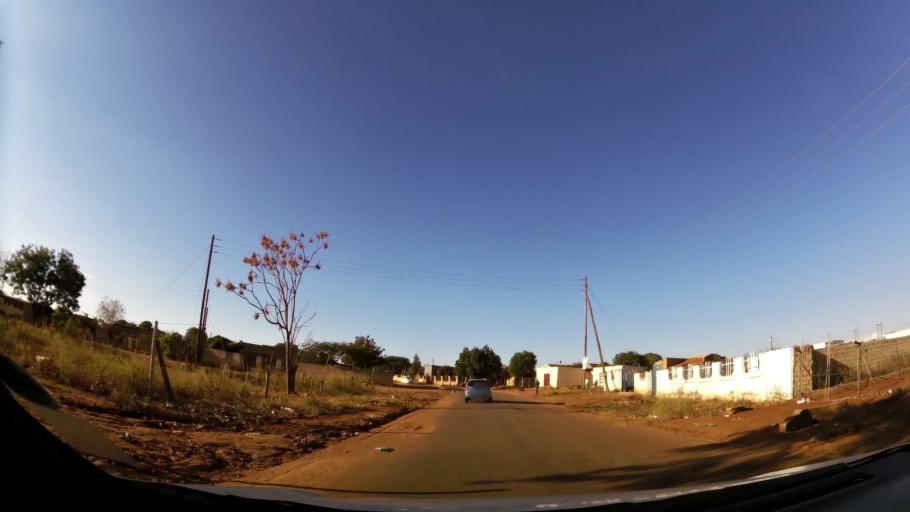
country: ZA
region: Limpopo
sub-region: Waterberg District Municipality
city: Mokopane
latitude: -24.1595
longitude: 28.9904
